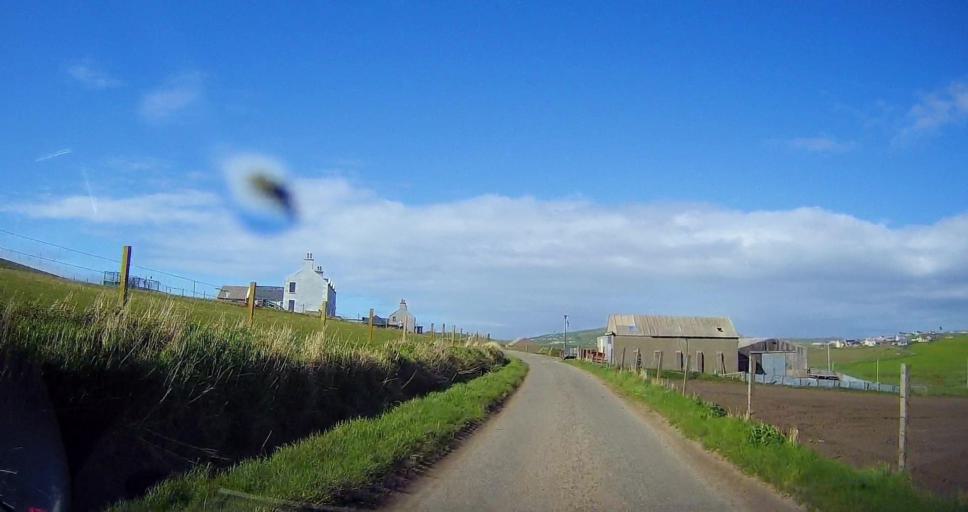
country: GB
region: Scotland
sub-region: Shetland Islands
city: Sandwick
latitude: 59.9074
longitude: -1.3343
